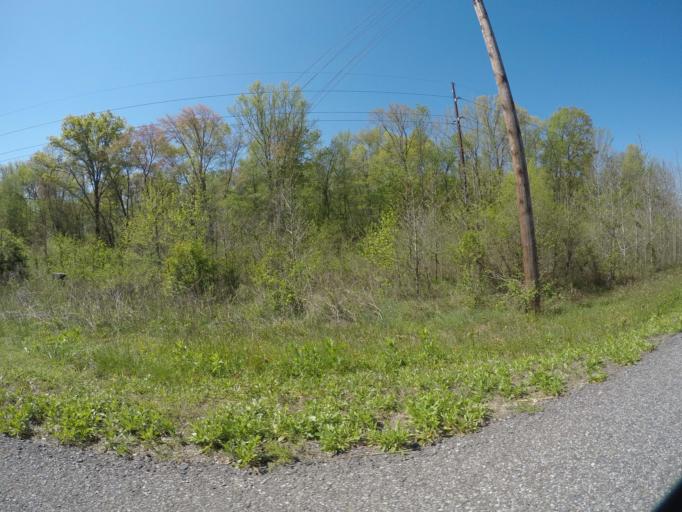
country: US
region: Maryland
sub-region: Charles County
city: Potomac Heights
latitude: 38.5933
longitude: -77.1227
